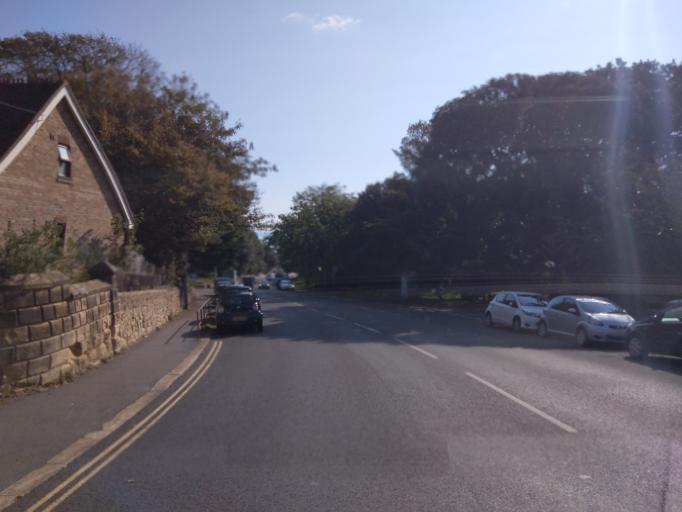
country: GB
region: England
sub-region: East Sussex
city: Hastings
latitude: 50.8582
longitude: 0.5658
